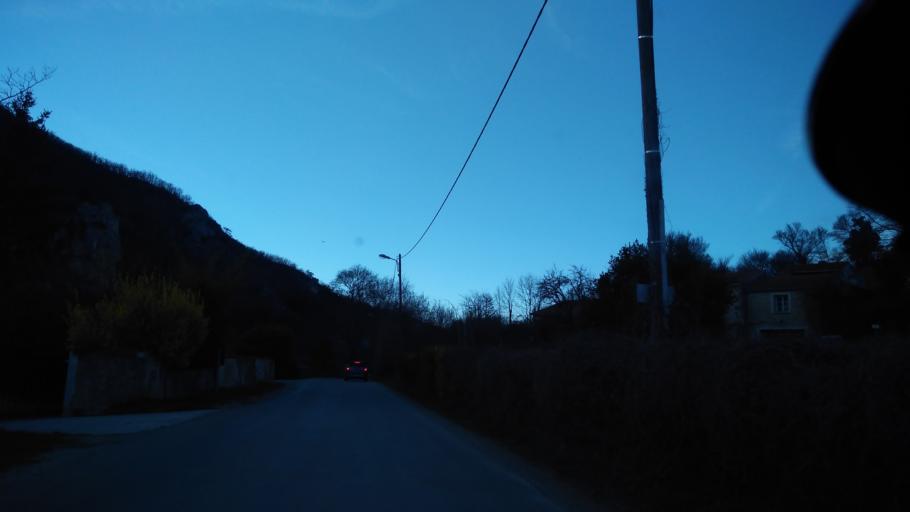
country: FR
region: Rhone-Alpes
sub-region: Departement de la Drome
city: Chabeuil
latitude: 44.8750
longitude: 5.0774
